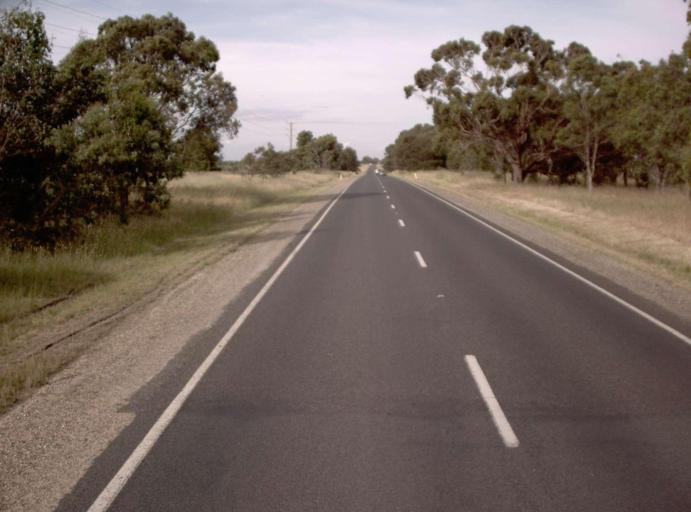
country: AU
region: Victoria
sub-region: Latrobe
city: Traralgon
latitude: -38.1176
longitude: 146.5776
